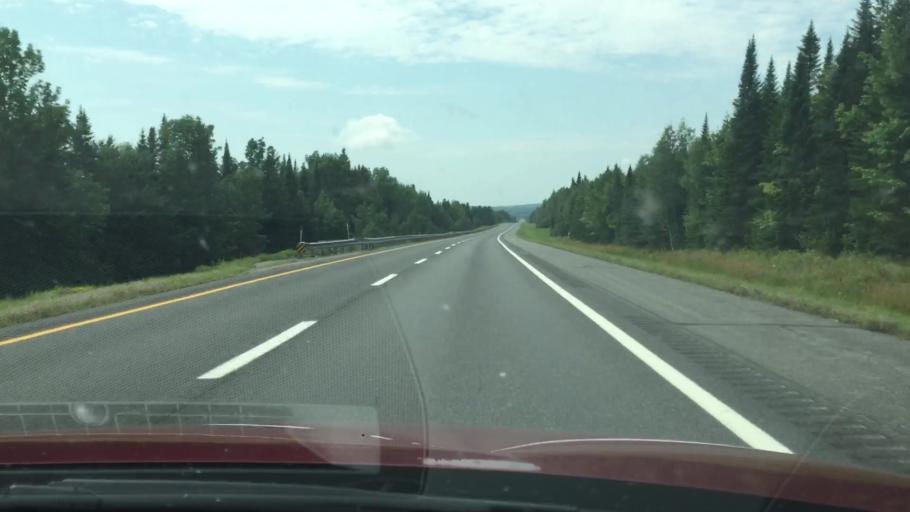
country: US
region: Maine
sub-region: Aroostook County
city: Hodgdon
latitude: 46.1195
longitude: -68.1213
